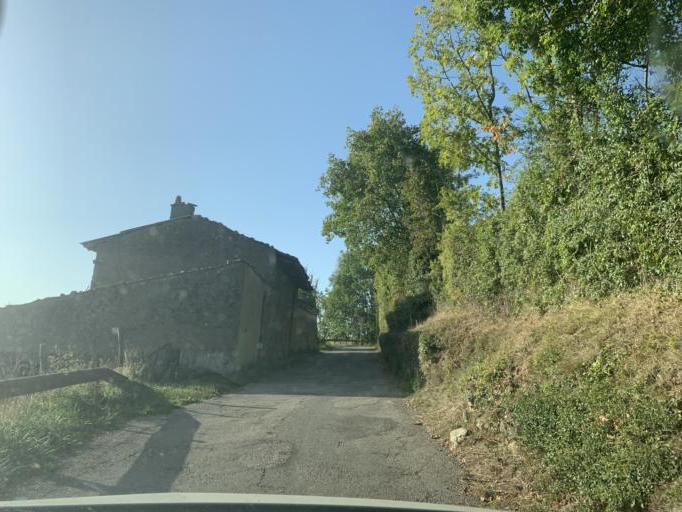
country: FR
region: Rhone-Alpes
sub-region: Departement de l'Ain
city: Amberieu-en-Bugey
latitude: 45.9500
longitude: 5.3690
